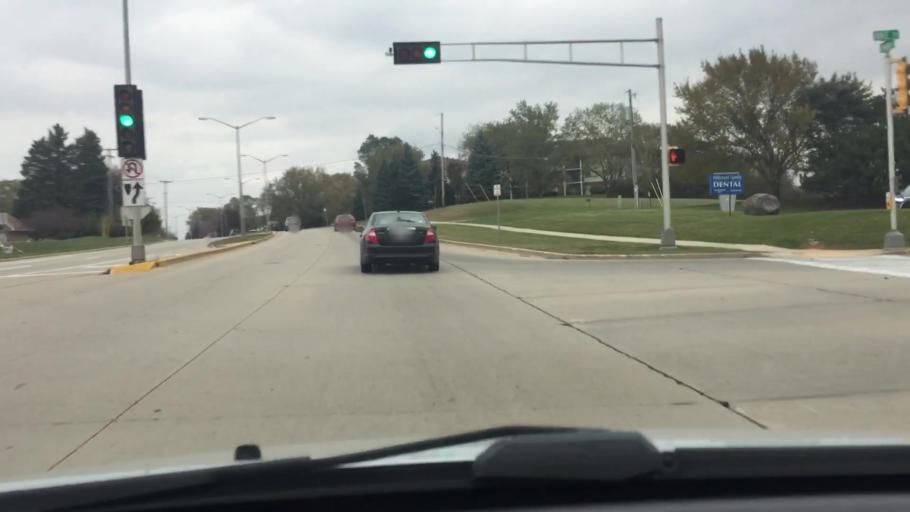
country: US
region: Wisconsin
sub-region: Waukesha County
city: Waukesha
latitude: 43.0221
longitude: -88.1973
